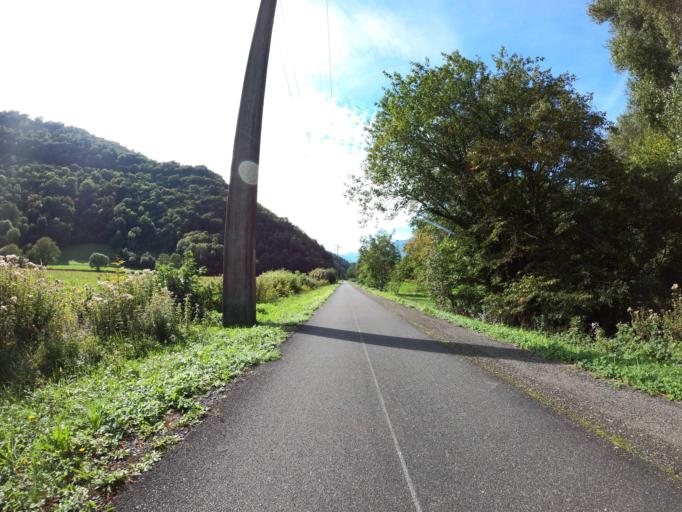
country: FR
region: Midi-Pyrenees
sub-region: Departement des Hautes-Pyrenees
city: Argeles-Gazost
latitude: 43.0380
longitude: -0.0606
